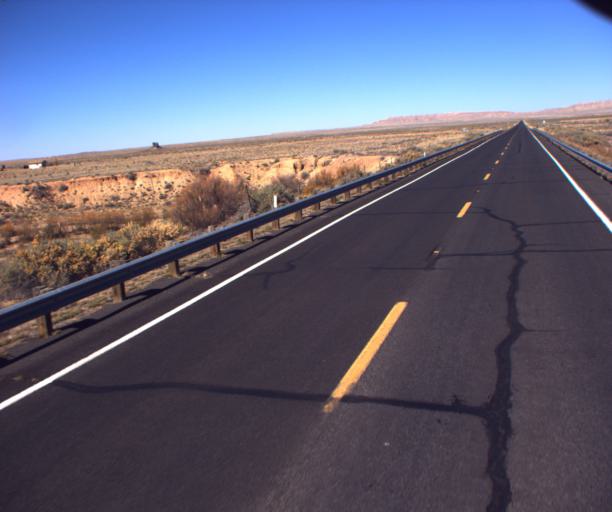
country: US
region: Arizona
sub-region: Navajo County
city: First Mesa
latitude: 35.7074
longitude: -110.5101
